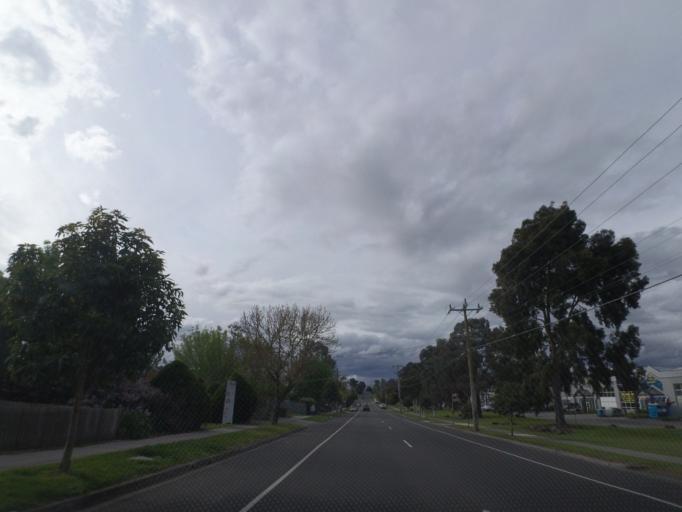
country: AU
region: Victoria
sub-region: Yarra Ranges
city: Lilydale
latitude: -37.7529
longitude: 145.3437
